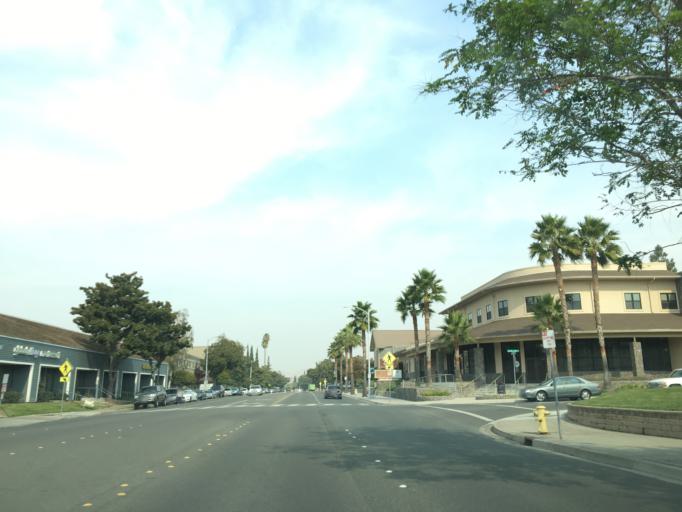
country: US
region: California
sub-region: Santa Clara County
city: Milpitas
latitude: 37.4190
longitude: -121.8759
